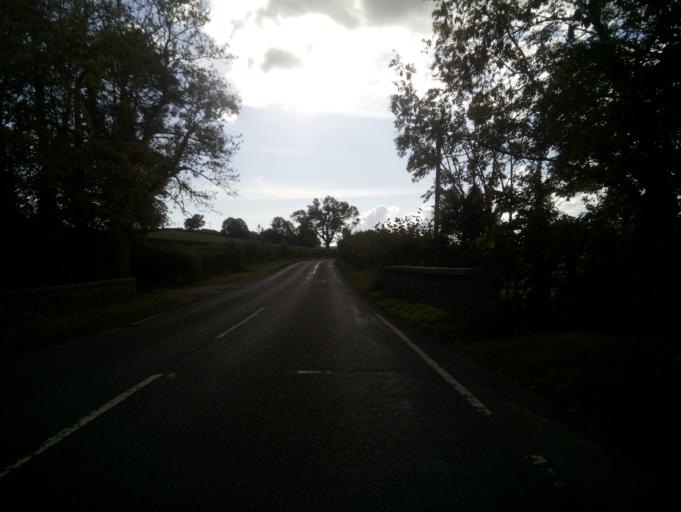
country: GB
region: Wales
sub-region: Sir Powys
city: Hay
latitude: 52.0551
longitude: -3.1701
